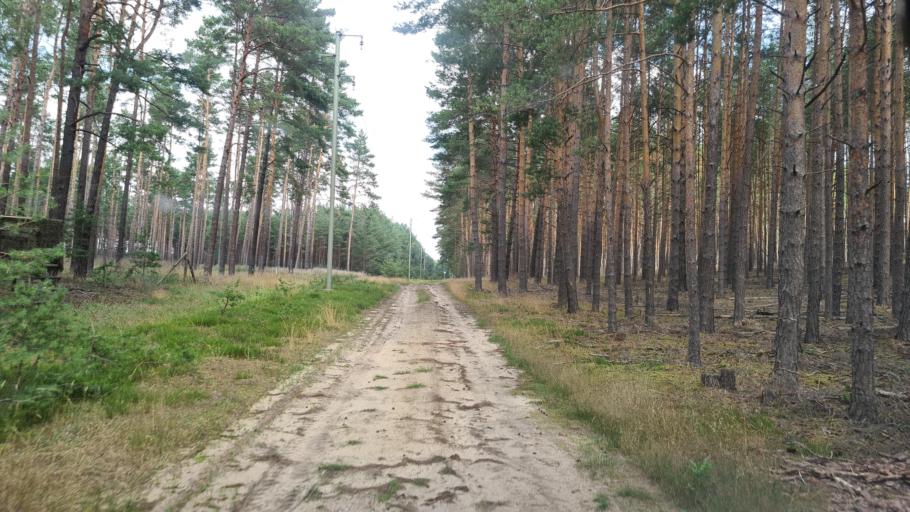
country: DE
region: Brandenburg
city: Bronkow
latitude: 51.6755
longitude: 13.8721
